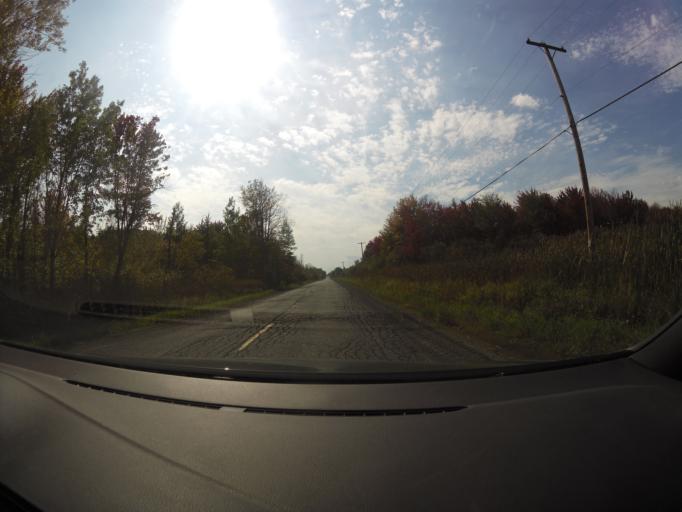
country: CA
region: Ontario
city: Bells Corners
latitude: 45.4268
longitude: -76.0125
